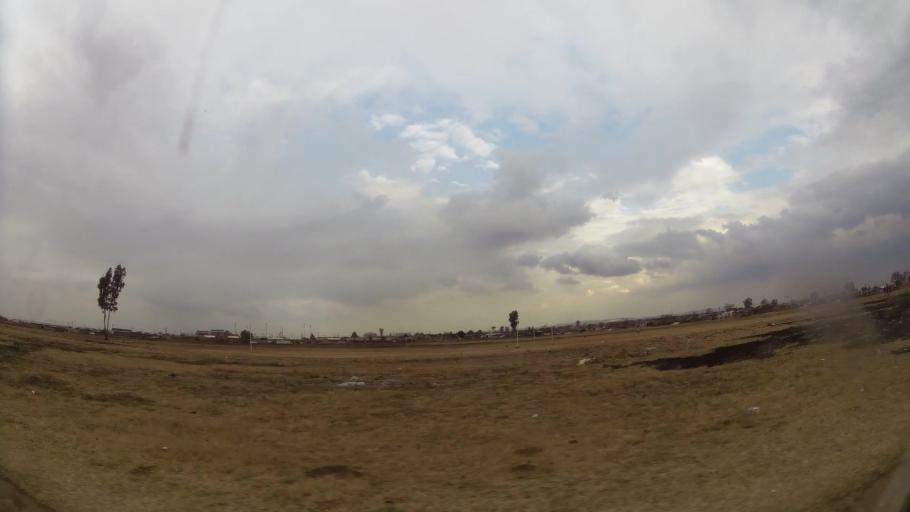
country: ZA
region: Gauteng
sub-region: Ekurhuleni Metropolitan Municipality
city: Germiston
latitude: -26.3839
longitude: 28.1338
